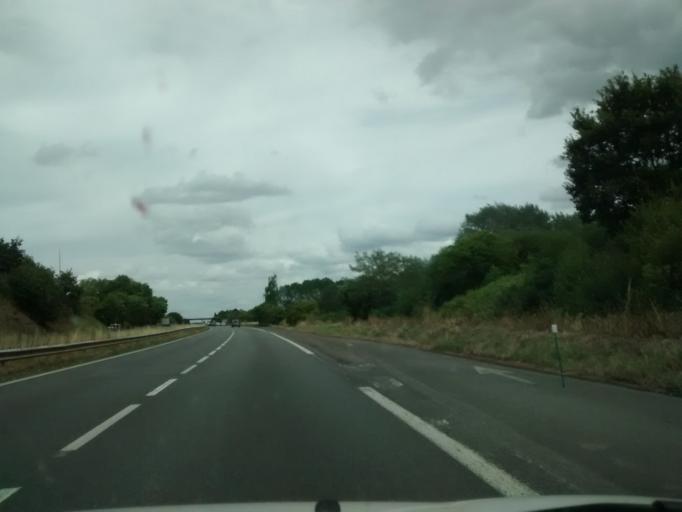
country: FR
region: Brittany
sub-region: Departement des Cotes-d'Armor
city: Yffiniac
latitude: 48.4791
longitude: -2.6643
